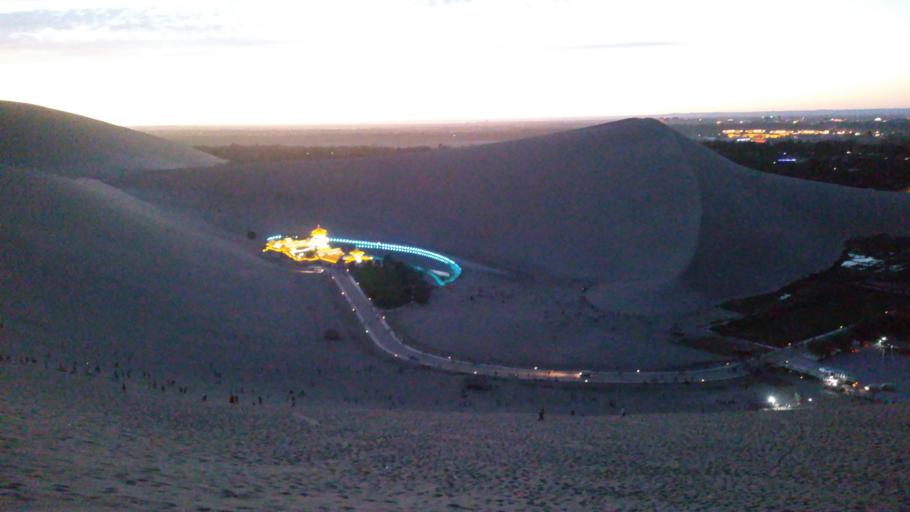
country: CN
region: Gansu Sheng
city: Yangjiaqiao
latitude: 40.0834
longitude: 94.6741
